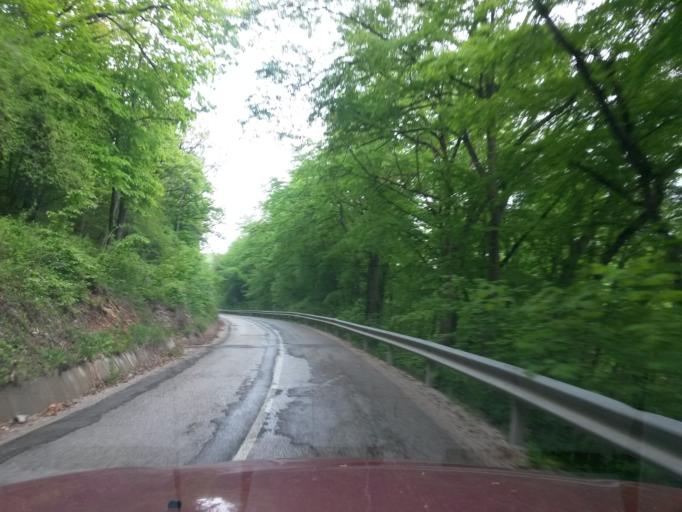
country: SK
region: Kosicky
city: Roznava
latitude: 48.5659
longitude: 20.4726
